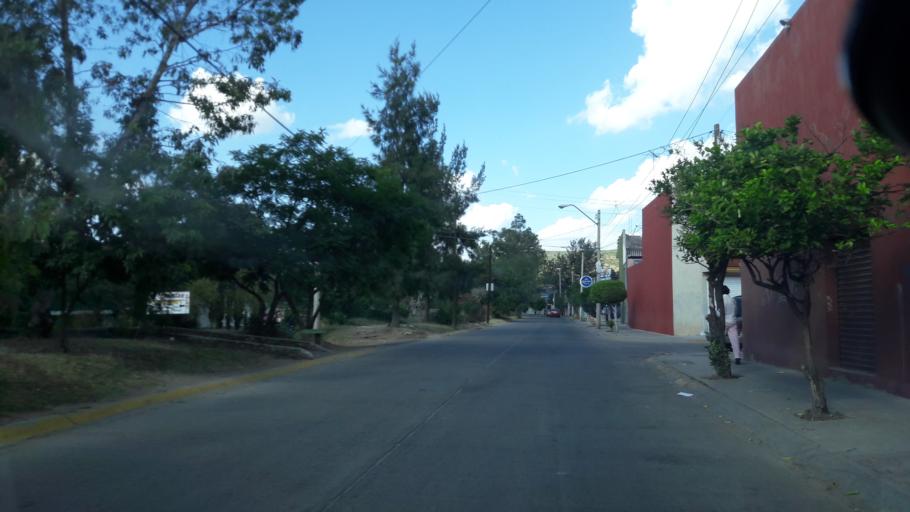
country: MX
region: Guanajuato
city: Leon
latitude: 21.1771
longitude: -101.6696
